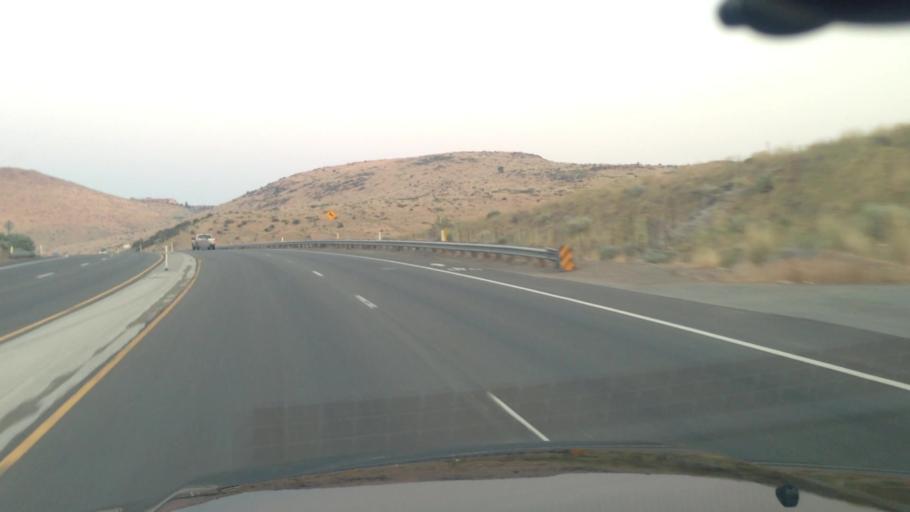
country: US
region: Nevada
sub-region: Washoe County
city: Reno
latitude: 39.4764
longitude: -119.8434
